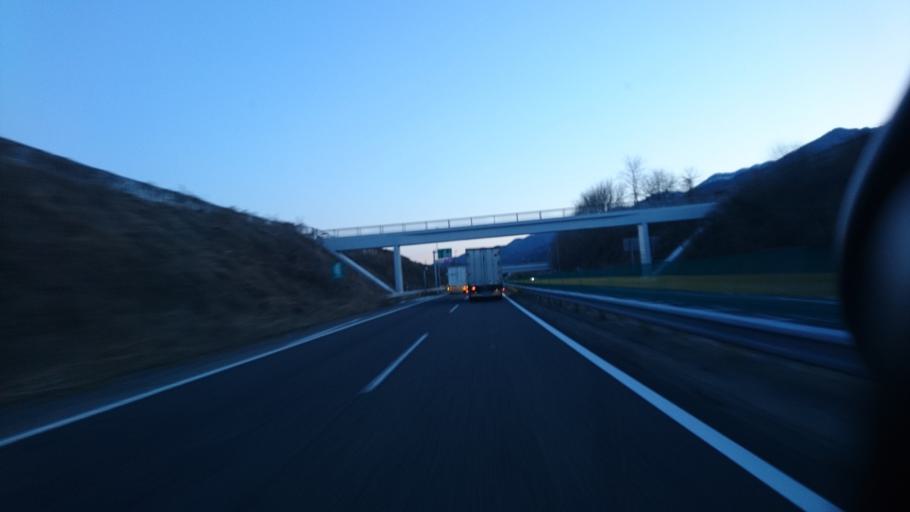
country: JP
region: Nagano
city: Ina
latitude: 35.8452
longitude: 137.9354
